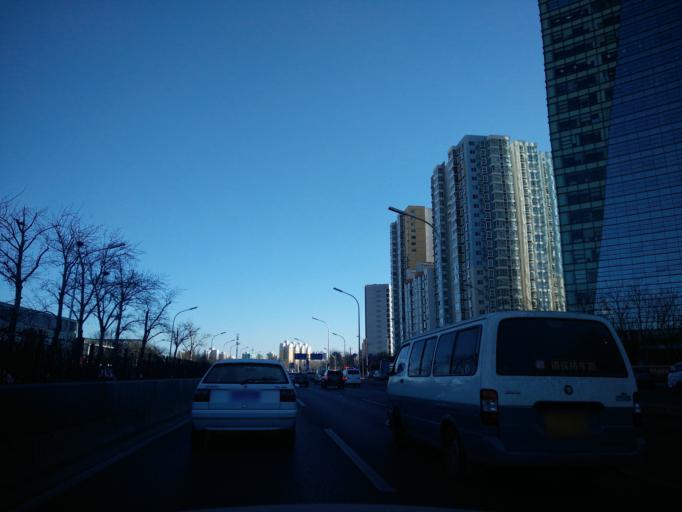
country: CN
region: Beijing
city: Baizhifang
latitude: 39.8543
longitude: 116.3613
